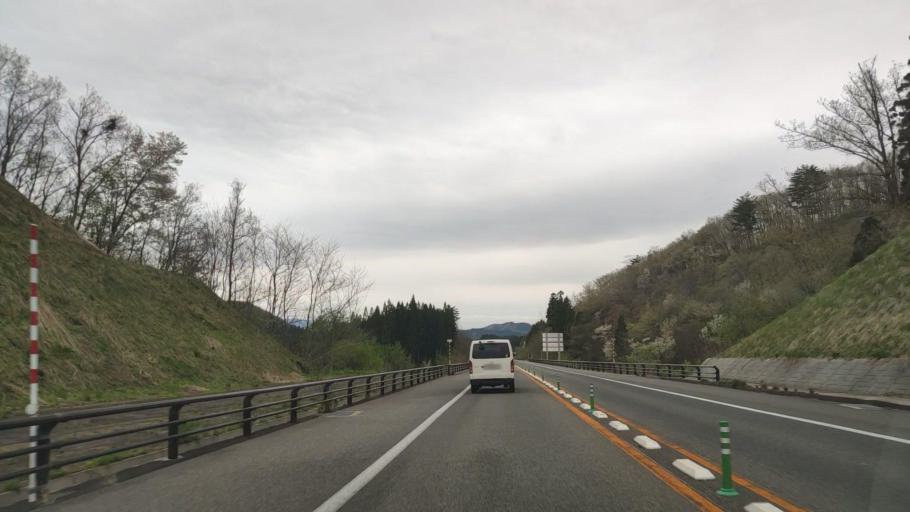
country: JP
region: Akita
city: Odate
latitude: 40.3191
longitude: 140.5899
